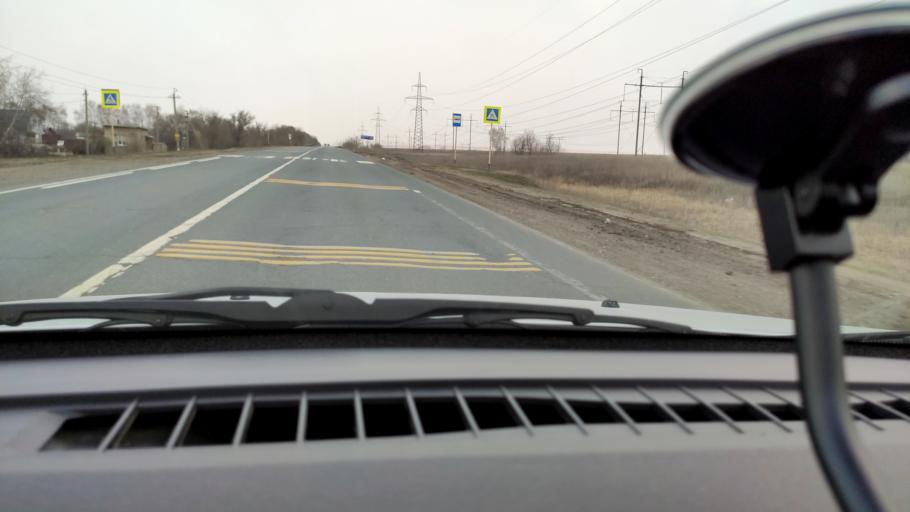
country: RU
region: Samara
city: Dubovyy Umet
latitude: 53.0710
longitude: 50.3825
